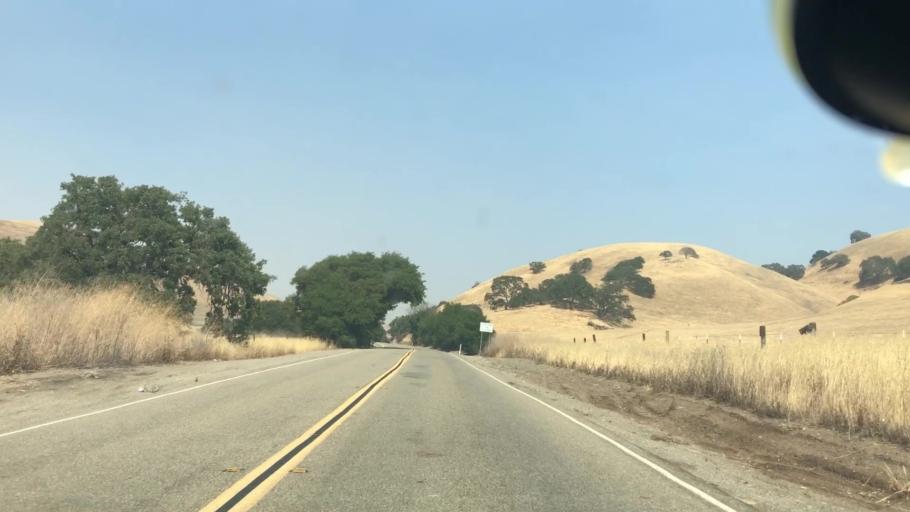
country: US
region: California
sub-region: Alameda County
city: Livermore
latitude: 37.6415
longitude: -121.6387
